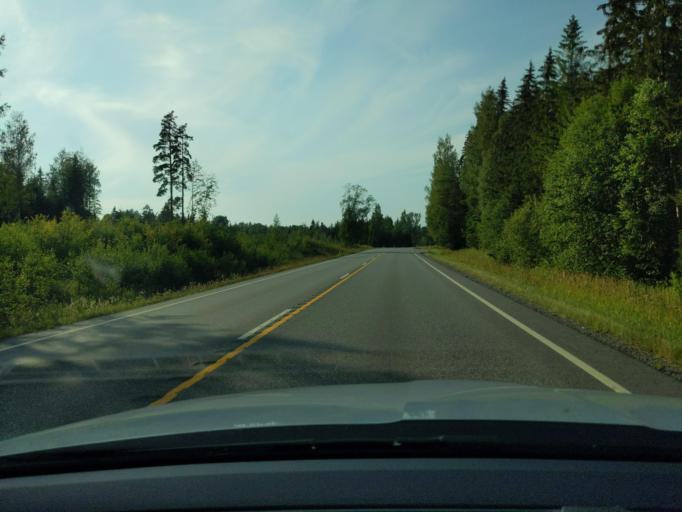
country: FI
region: Paijanne Tavastia
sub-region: Lahti
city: Padasjoki
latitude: 61.3196
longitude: 25.2835
